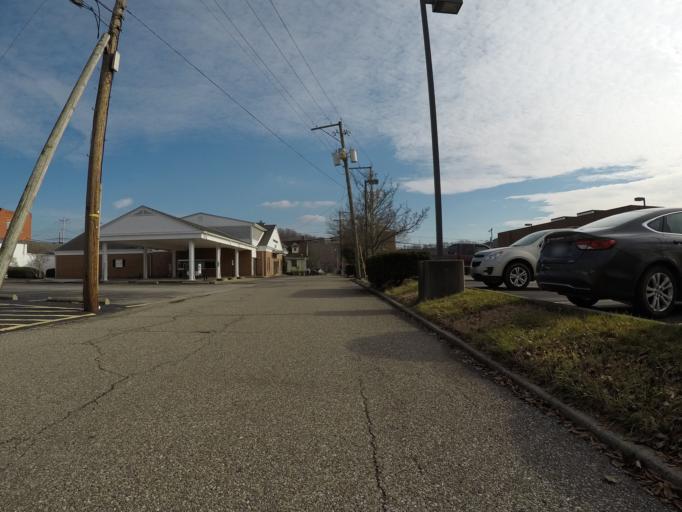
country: US
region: West Virginia
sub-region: Cabell County
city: Barboursville
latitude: 38.4091
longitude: -82.2962
